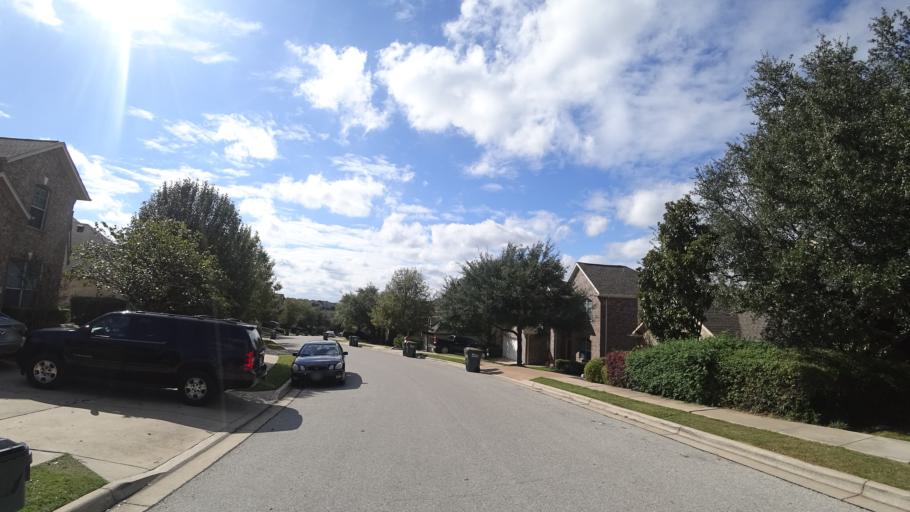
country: US
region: Texas
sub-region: Travis County
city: Hudson Bend
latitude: 30.3629
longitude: -97.9009
